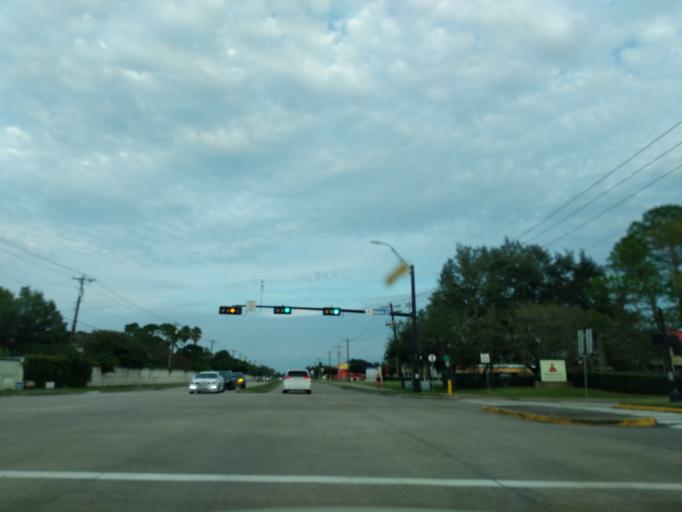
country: US
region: Texas
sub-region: Galveston County
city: Clear Lake Shores
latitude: 29.5261
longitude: -95.0486
